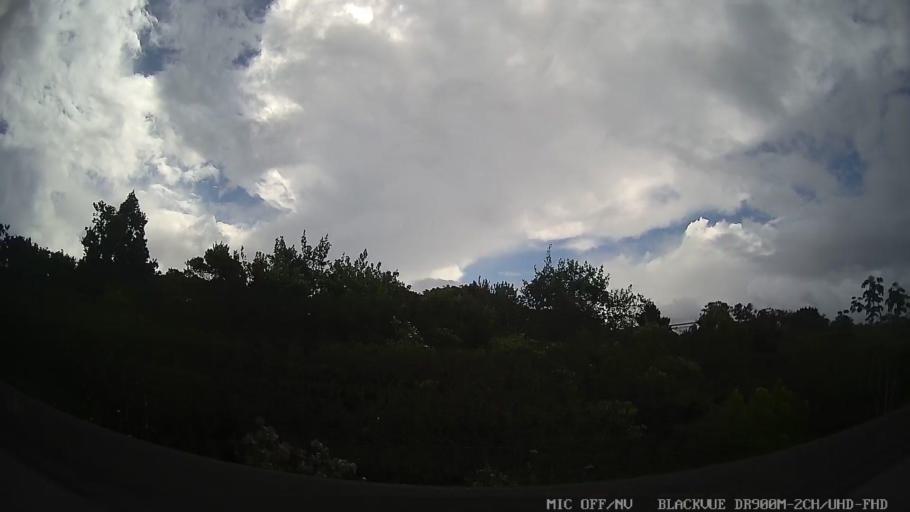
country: BR
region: Sao Paulo
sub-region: Peruibe
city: Peruibe
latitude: -24.2612
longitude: -46.9471
